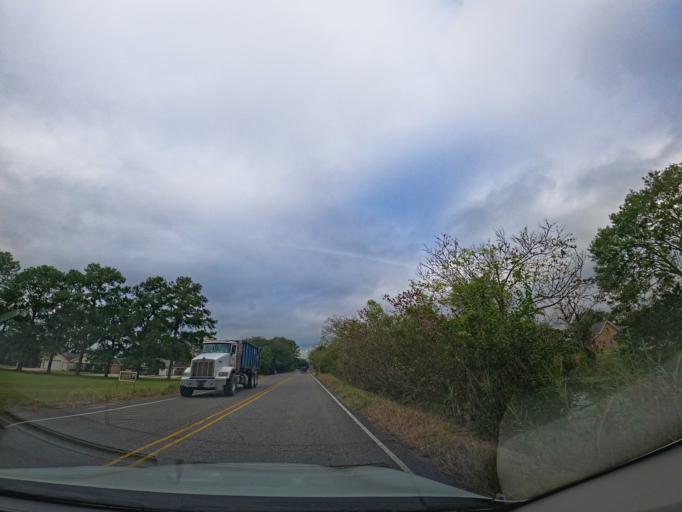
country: US
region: Louisiana
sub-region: Terrebonne Parish
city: Houma
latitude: 29.5739
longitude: -90.7573
